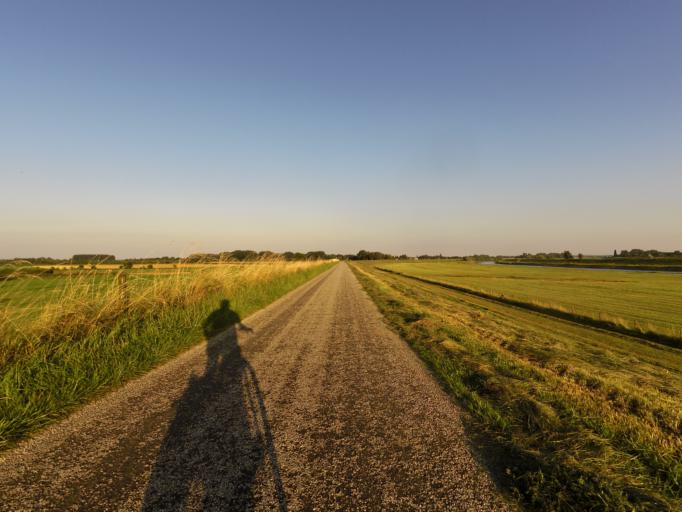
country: NL
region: Gelderland
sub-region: Gemeente Duiven
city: Duiven
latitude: 51.9064
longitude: 6.0122
